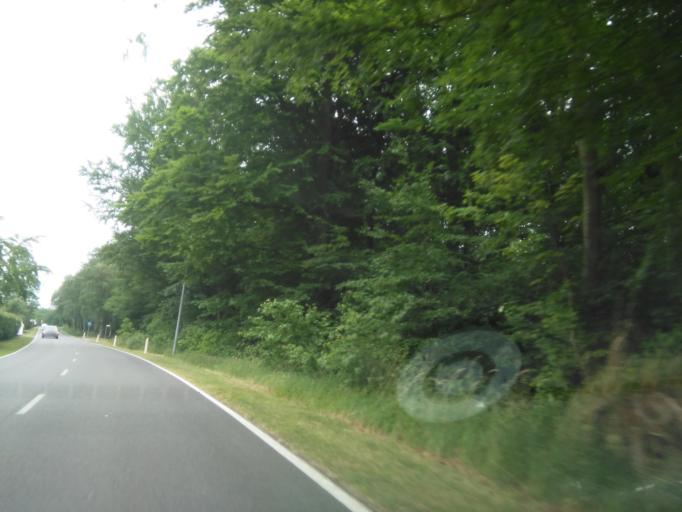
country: DK
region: Capital Region
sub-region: Bornholm Kommune
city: Ronne
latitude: 55.0810
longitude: 14.7250
